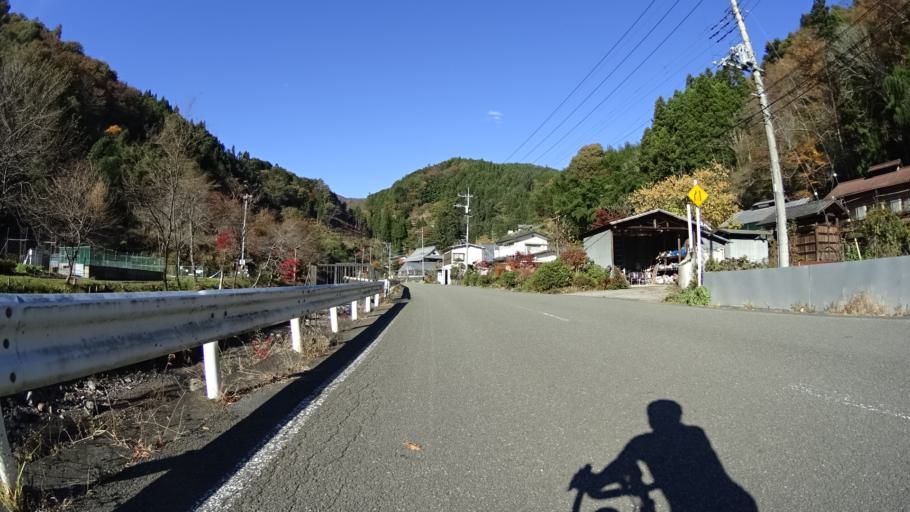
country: JP
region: Yamanashi
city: Otsuki
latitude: 35.7084
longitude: 139.0066
